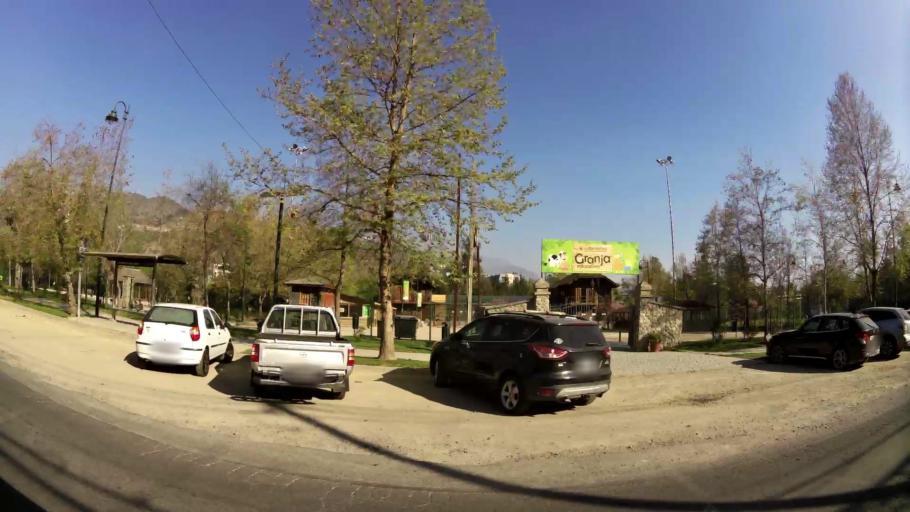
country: CL
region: Santiago Metropolitan
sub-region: Provincia de Santiago
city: Villa Presidente Frei, Nunoa, Santiago, Chile
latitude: -33.3620
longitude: -70.4972
